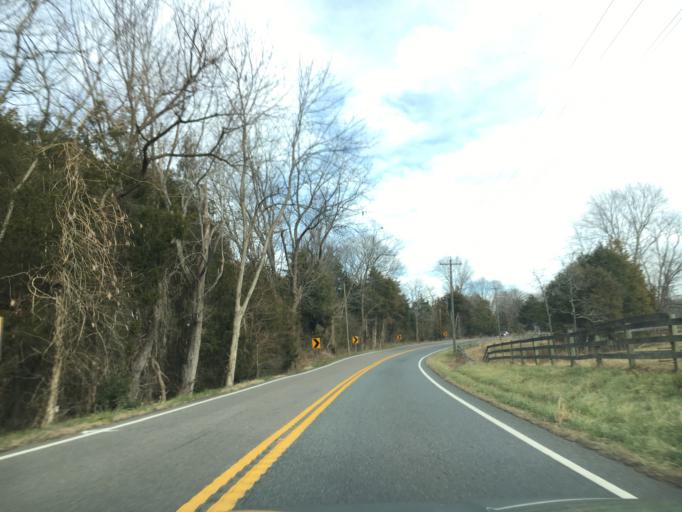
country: US
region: Virginia
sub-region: Goochland County
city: Goochland
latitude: 37.7964
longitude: -77.8715
